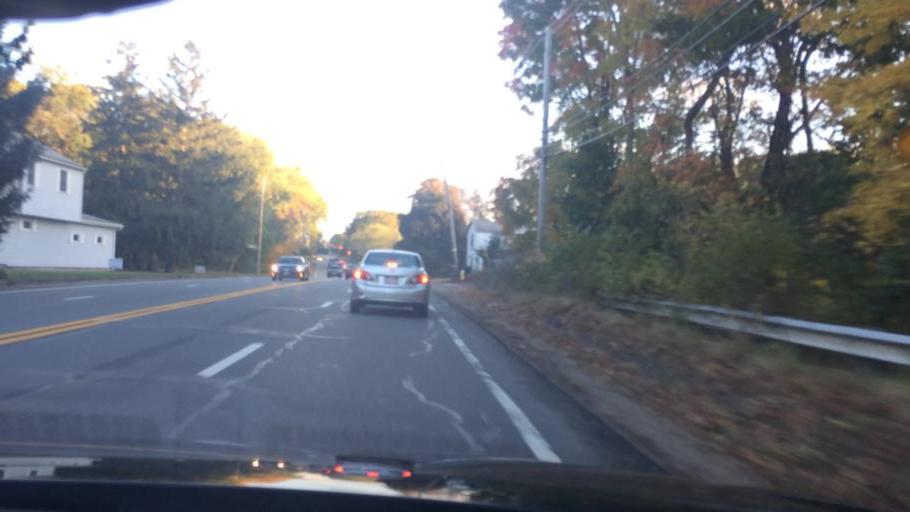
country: US
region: Massachusetts
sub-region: Middlesex County
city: Chelmsford
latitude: 42.6294
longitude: -71.3722
